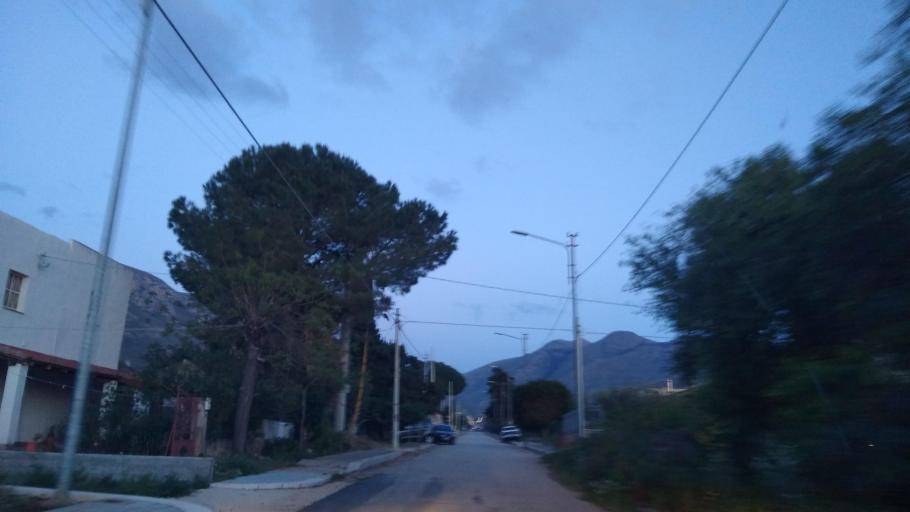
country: IT
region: Sicily
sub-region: Trapani
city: Castelluzzo
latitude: 38.1050
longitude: 12.7311
